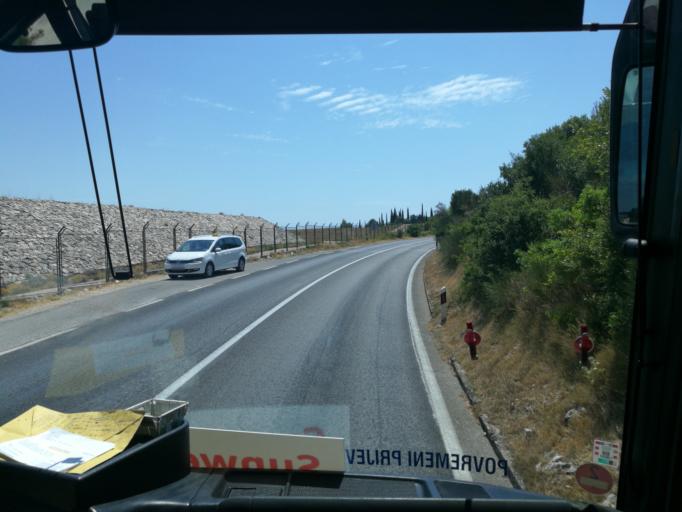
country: HR
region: Dubrovacko-Neretvanska
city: Cavtat
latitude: 42.5701
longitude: 18.2452
